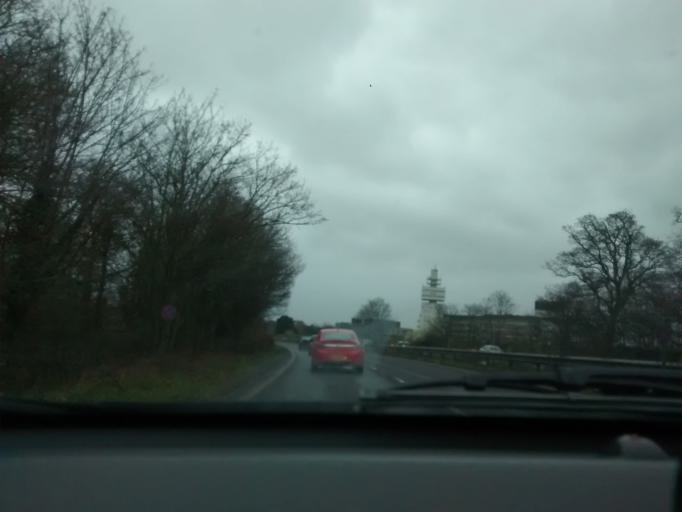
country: GB
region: England
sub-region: Suffolk
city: Kesgrave
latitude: 52.0514
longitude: 1.2776
